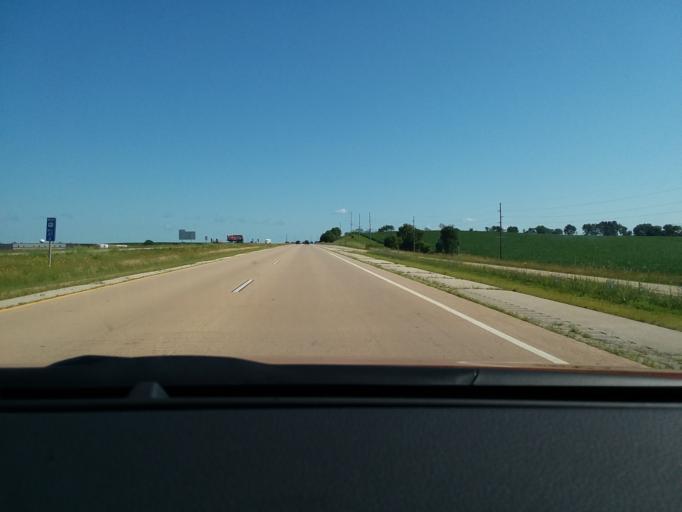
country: US
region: Wisconsin
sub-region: Dane County
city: Windsor
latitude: 43.1970
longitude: -89.3242
